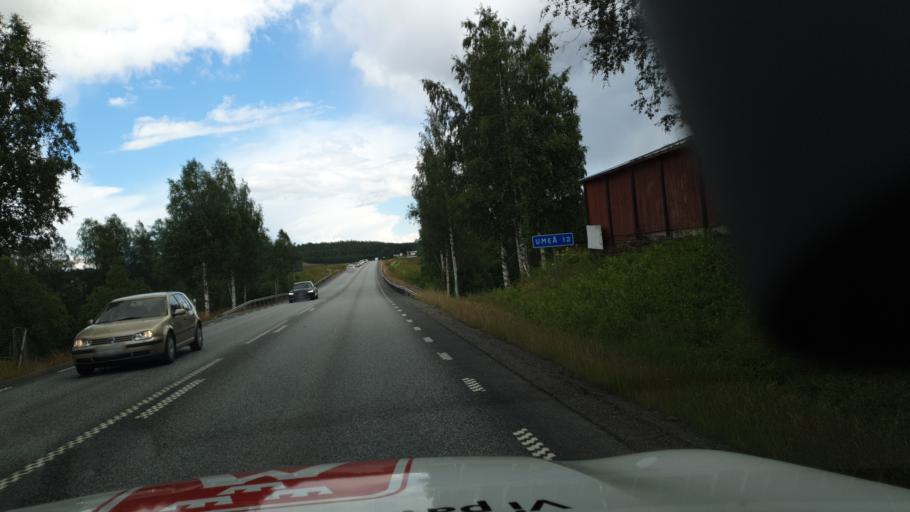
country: SE
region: Vaesterbotten
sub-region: Umea Kommun
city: Roback
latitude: 63.8741
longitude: 20.0681
